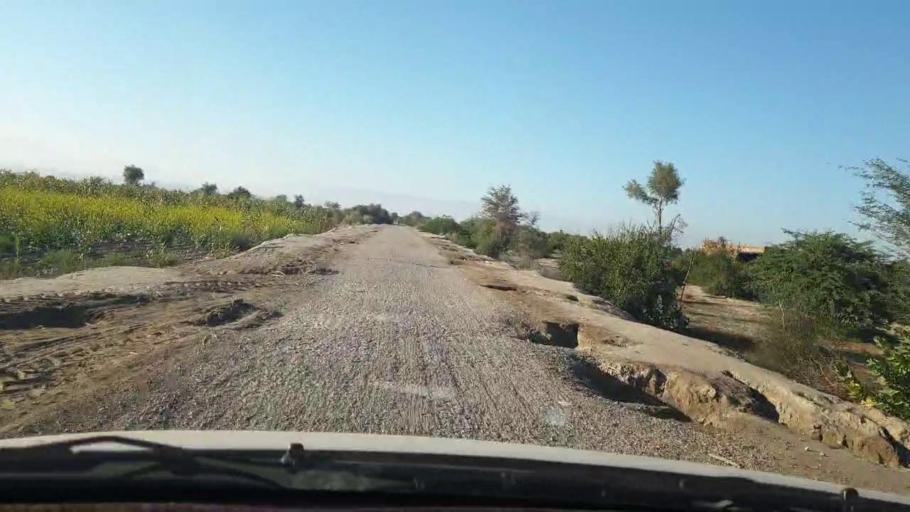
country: PK
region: Sindh
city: Johi
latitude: 26.7706
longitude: 67.4583
